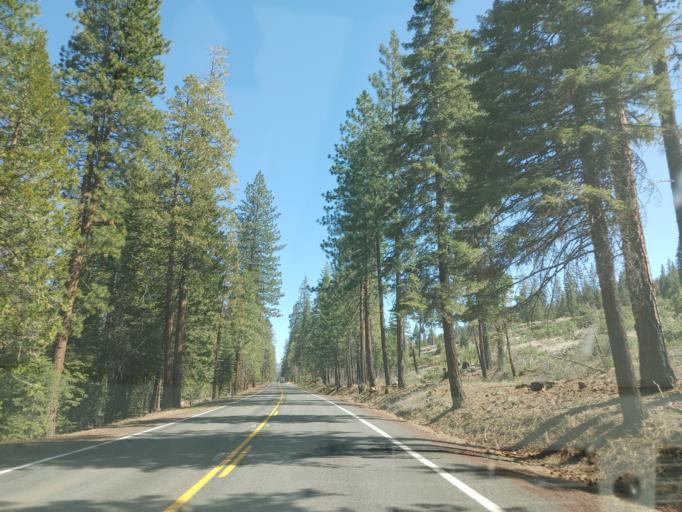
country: US
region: California
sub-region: Shasta County
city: Burney
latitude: 40.7582
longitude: -121.4971
